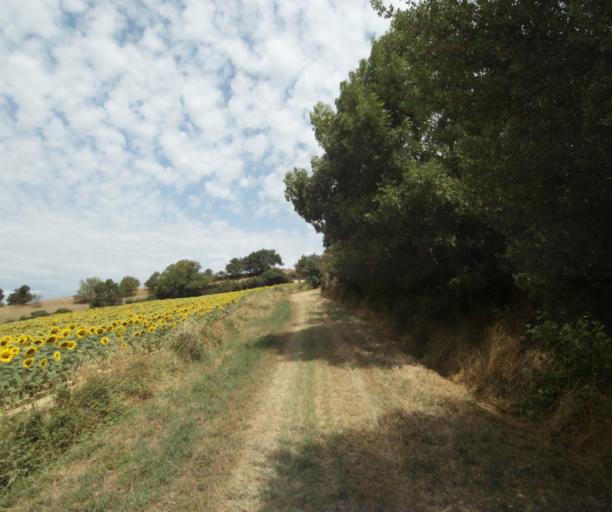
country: FR
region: Midi-Pyrenees
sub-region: Departement de la Haute-Garonne
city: Saint-Felix-Lauragais
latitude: 43.4392
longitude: 1.8925
